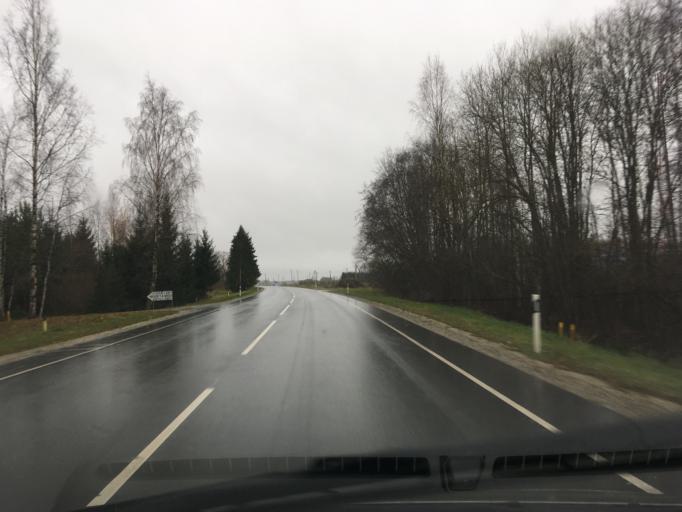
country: EE
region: Harju
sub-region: Nissi vald
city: Turba
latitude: 58.8870
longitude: 24.0910
